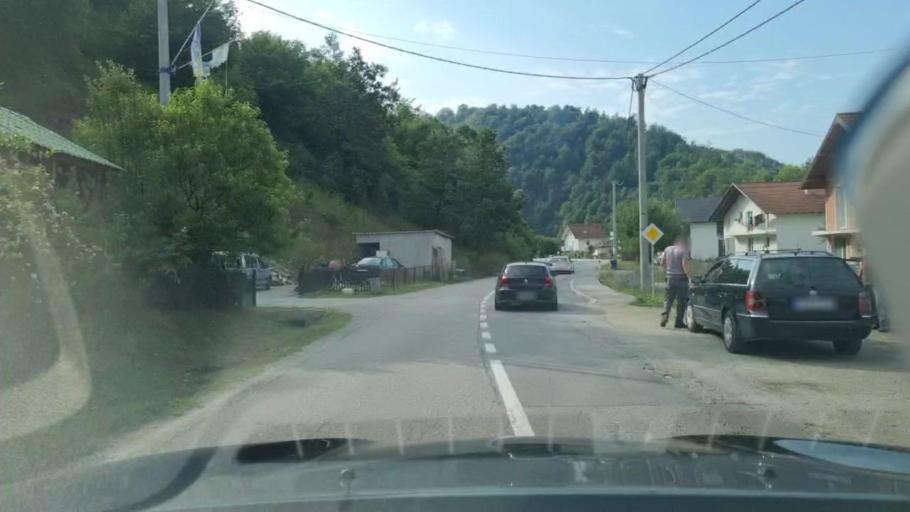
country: BA
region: Federation of Bosnia and Herzegovina
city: Jezerski
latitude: 45.0087
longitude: 16.1088
